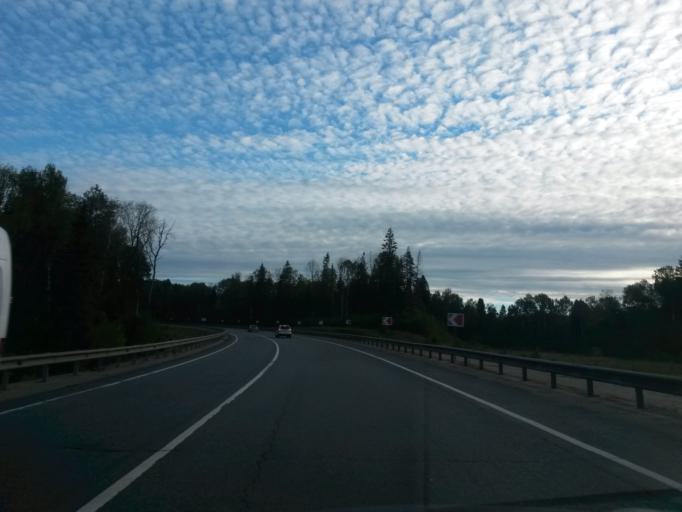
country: RU
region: Vladimir
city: Strunino
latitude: 56.5460
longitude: 38.5942
